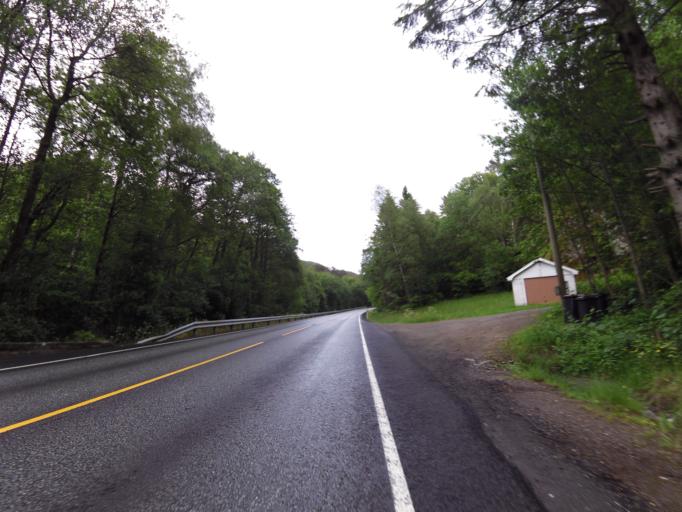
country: NO
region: Vest-Agder
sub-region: Farsund
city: Farsund
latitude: 58.1020
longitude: 6.8814
